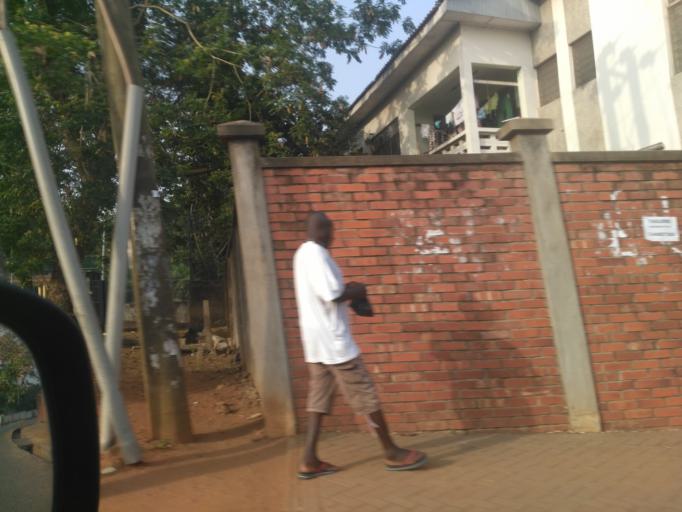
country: GH
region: Greater Accra
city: Accra
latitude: 5.6040
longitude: -0.1942
